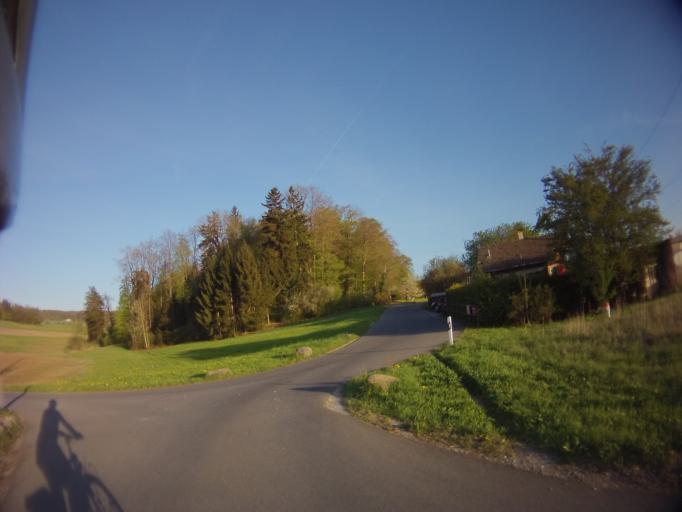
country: CH
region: Zurich
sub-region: Bezirk Affoltern
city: Obfelden / Toussen
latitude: 47.2600
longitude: 8.4430
